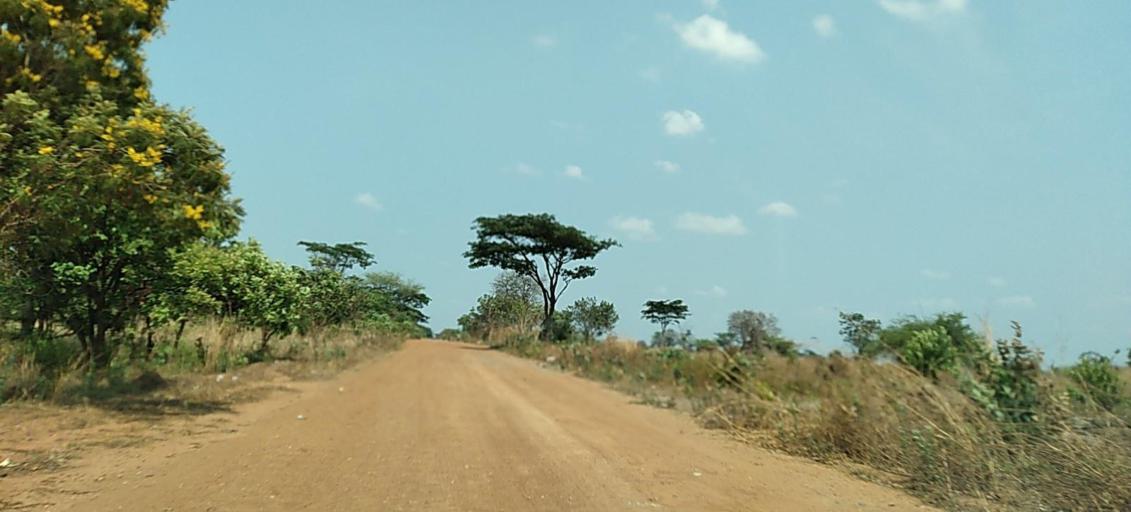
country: ZM
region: Copperbelt
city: Luanshya
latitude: -13.0914
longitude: 28.2921
